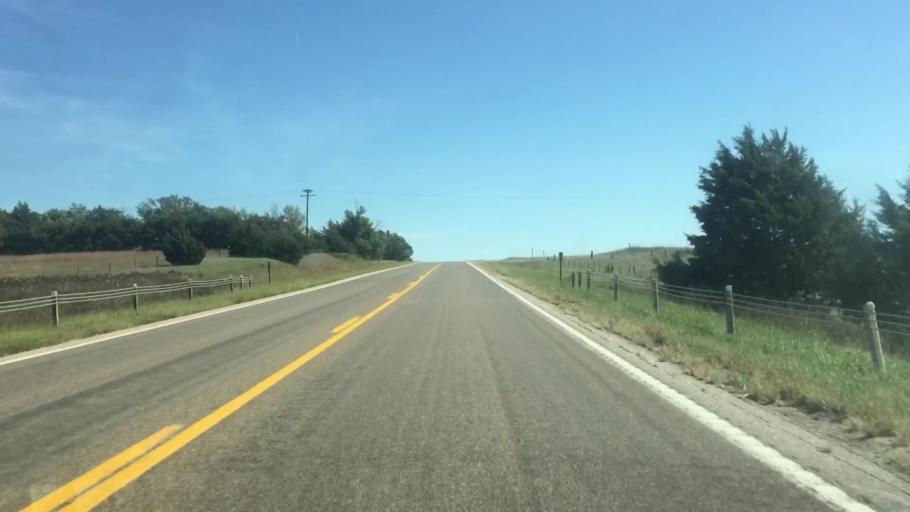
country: US
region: Nebraska
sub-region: Thayer County
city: Hebron
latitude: 40.1472
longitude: -97.5403
